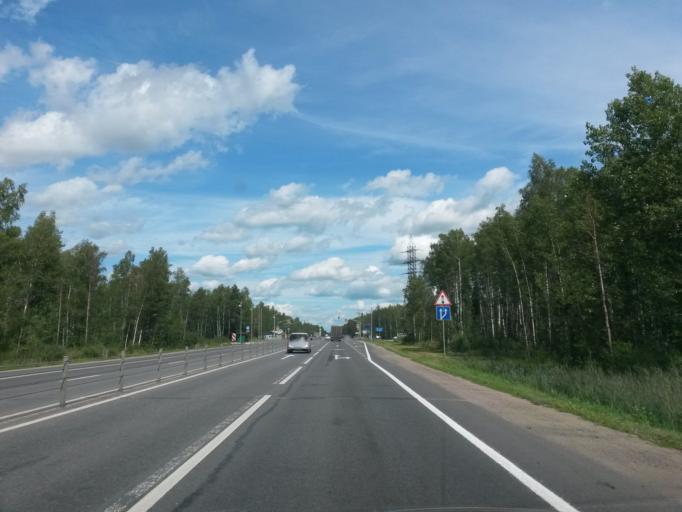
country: RU
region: Jaroslavl
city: Rostov
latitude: 57.2348
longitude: 39.4708
